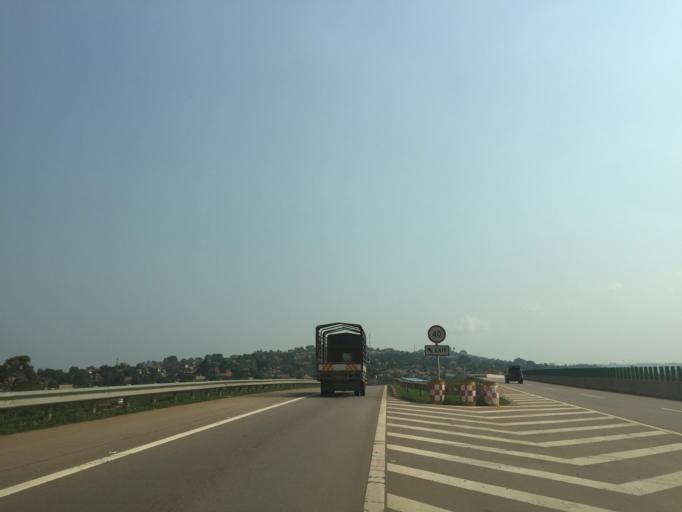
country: UG
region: Central Region
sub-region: Wakiso District
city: Kajansi
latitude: 0.2176
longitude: 32.5312
